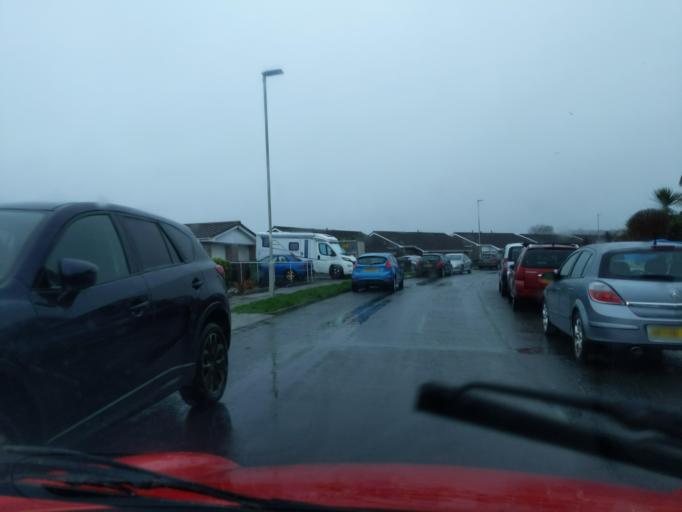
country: GB
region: England
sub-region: Plymouth
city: Plymstock
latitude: 50.3988
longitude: -4.1063
